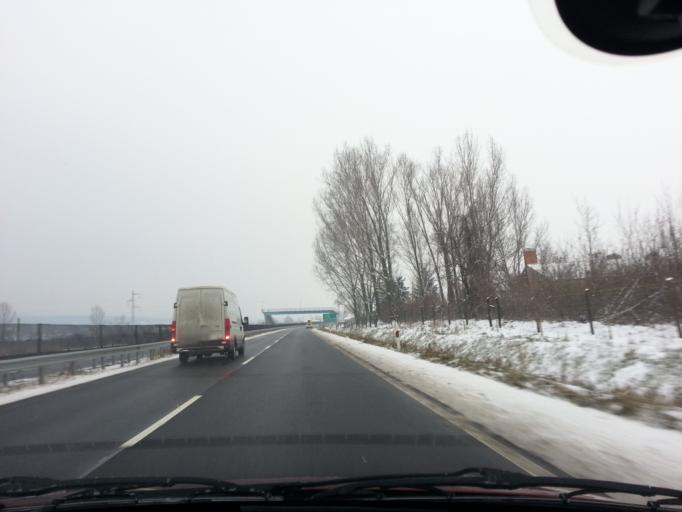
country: HU
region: Nograd
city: Jobbagyi
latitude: 47.8341
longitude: 19.6812
